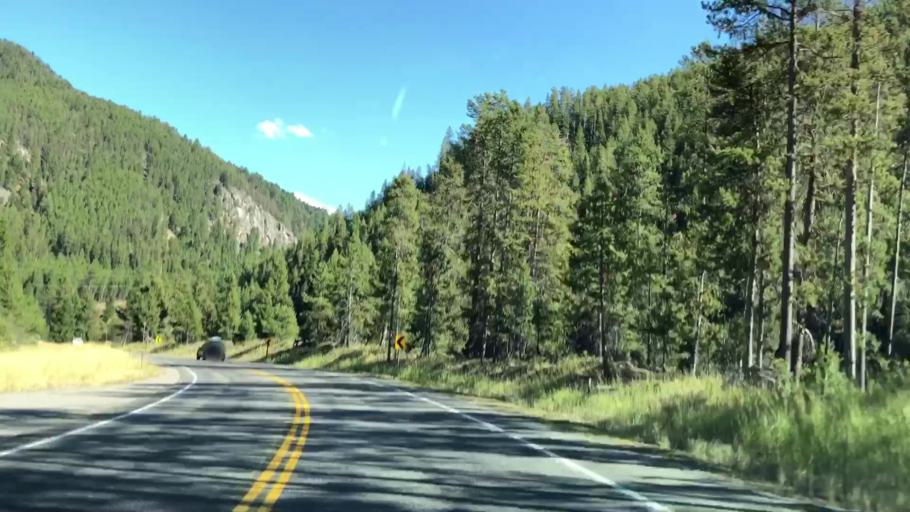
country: US
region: Montana
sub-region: Gallatin County
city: Big Sky
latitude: 45.3906
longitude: -111.2035
